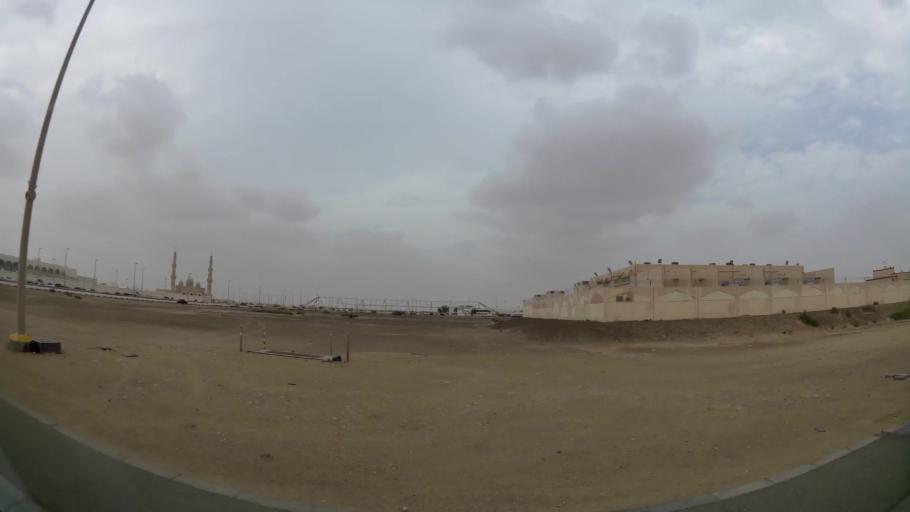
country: AE
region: Abu Dhabi
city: Abu Dhabi
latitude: 24.3508
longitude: 54.6515
